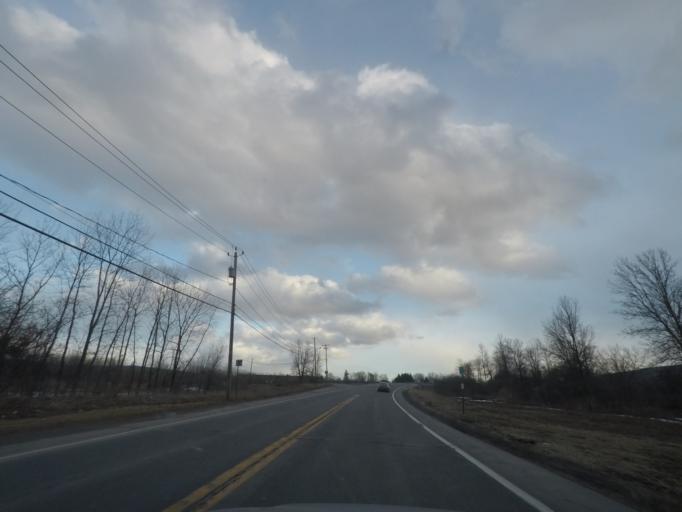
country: US
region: New York
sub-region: Herkimer County
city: Frankfort
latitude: 43.0870
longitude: -75.1251
